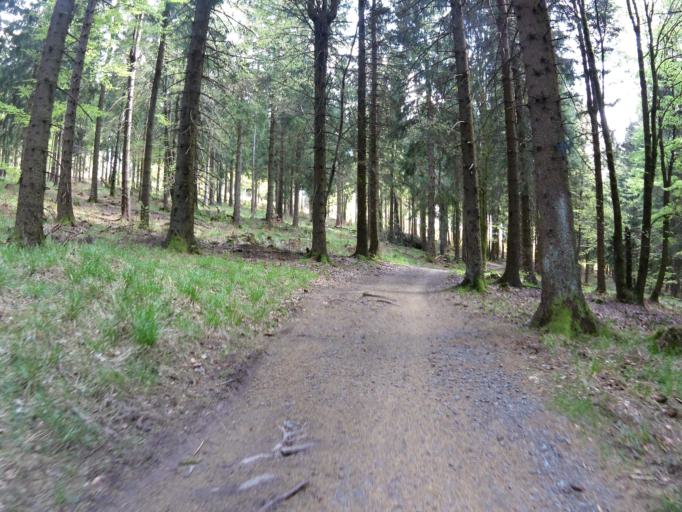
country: DE
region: Thuringia
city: Finsterbergen
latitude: 50.8061
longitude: 10.5448
